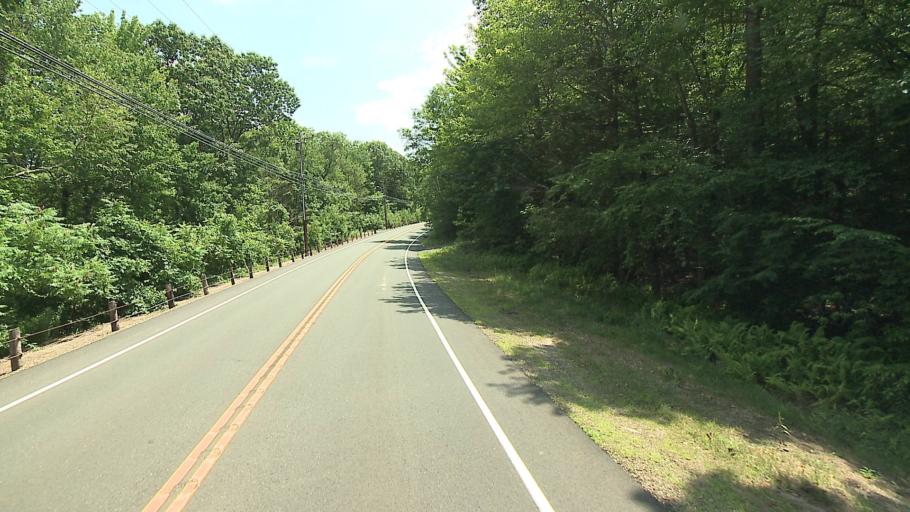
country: US
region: Connecticut
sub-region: Hartford County
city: North Granby
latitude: 41.9951
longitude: -72.8683
